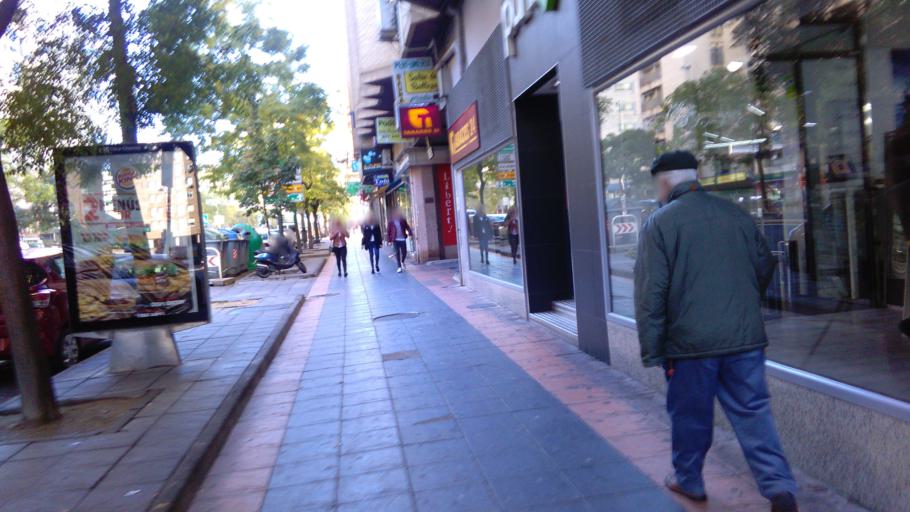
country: ES
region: Extremadura
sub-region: Provincia de Caceres
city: Caceres
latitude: 39.4678
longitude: -6.3798
